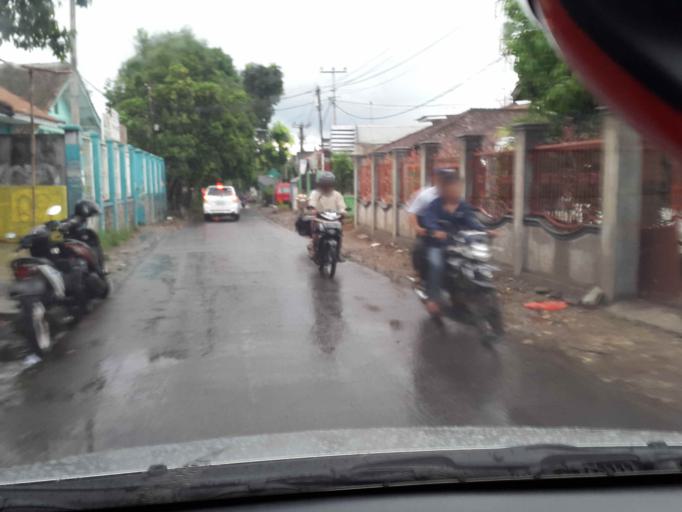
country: ID
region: West Java
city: Sukabumi
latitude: -6.9139
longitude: 106.8857
